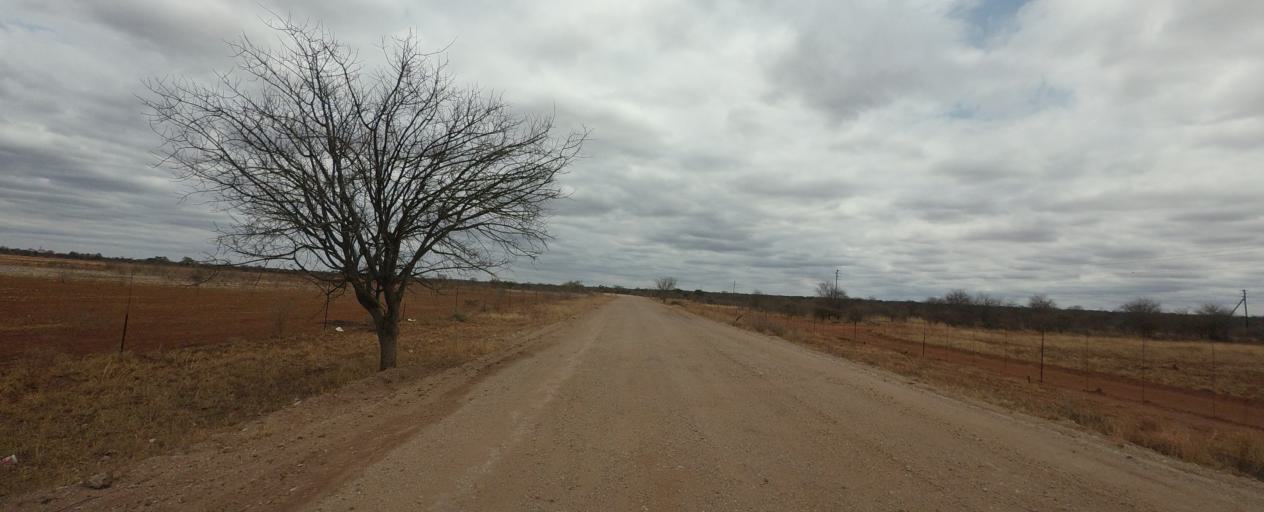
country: BW
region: Central
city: Mathathane
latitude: -22.7108
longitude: 28.5679
